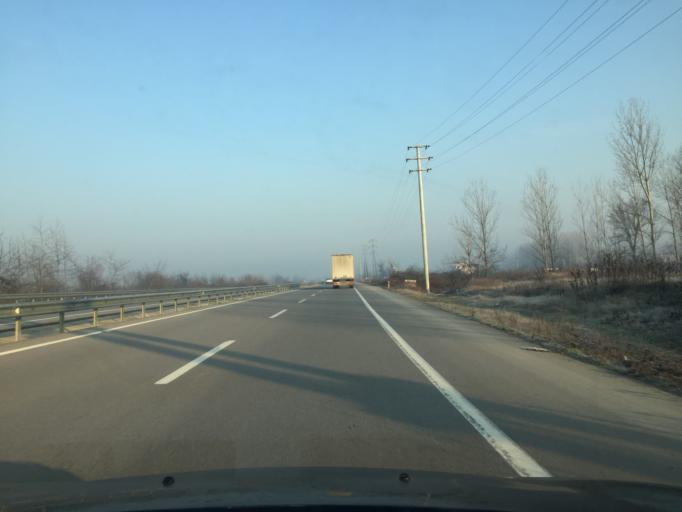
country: TR
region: Sakarya
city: Akyazi
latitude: 40.6997
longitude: 30.5679
